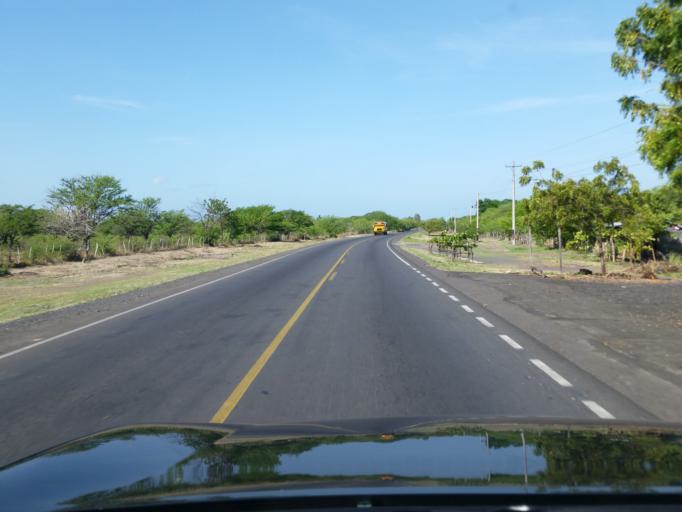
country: NI
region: Leon
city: La Paz Centro
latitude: 12.2873
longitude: -86.7198
